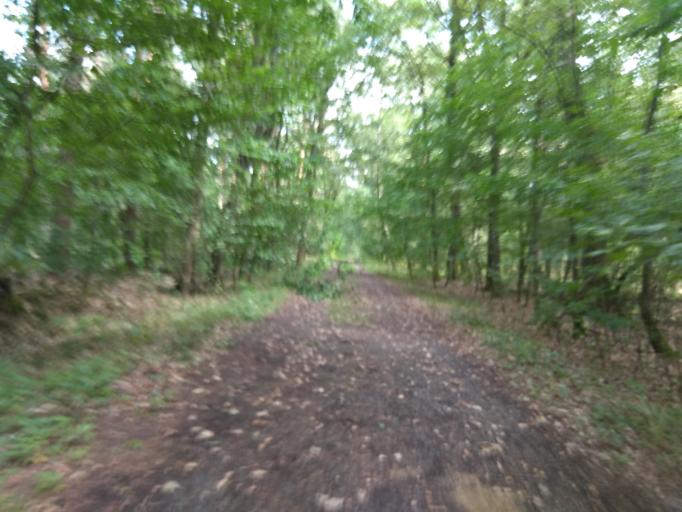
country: DE
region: North Rhine-Westphalia
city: Marl
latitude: 51.7030
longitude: 7.0497
